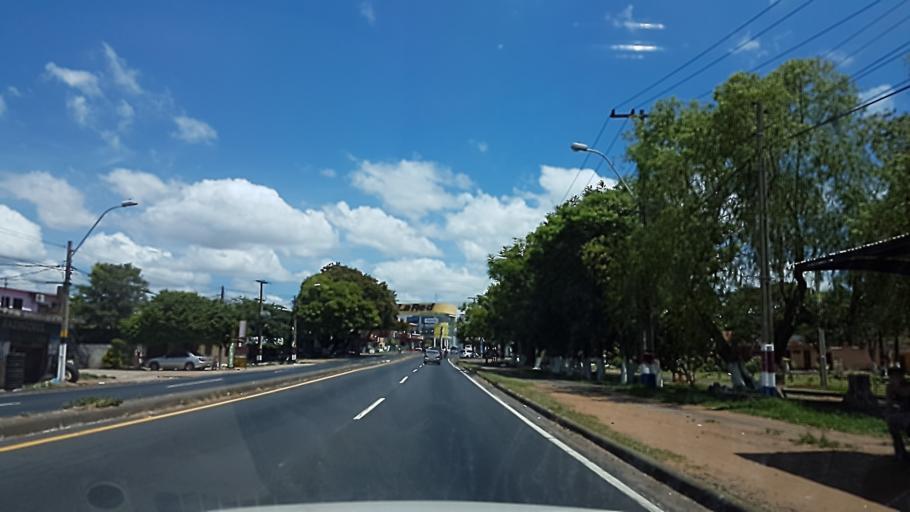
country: PY
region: Central
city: Capiata
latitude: -25.3582
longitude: -57.4374
